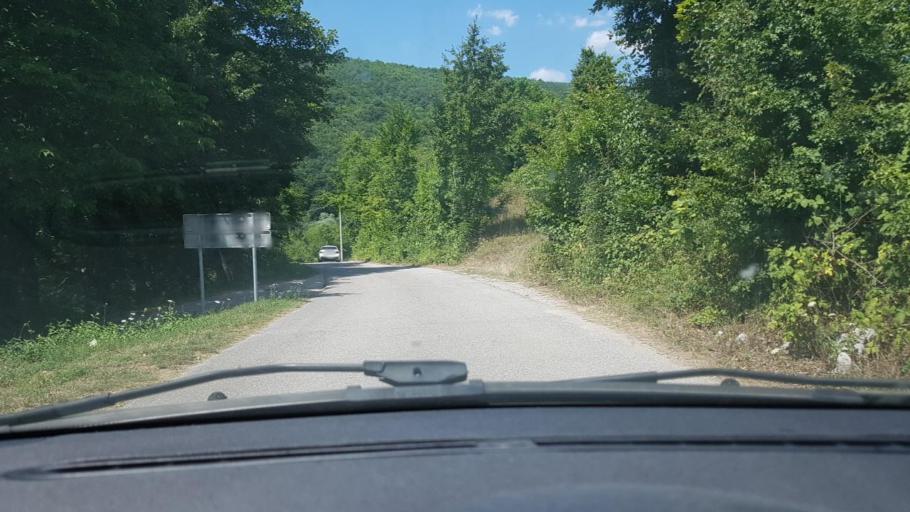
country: BA
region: Federation of Bosnia and Herzegovina
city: Orasac
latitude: 44.4944
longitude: 16.1385
